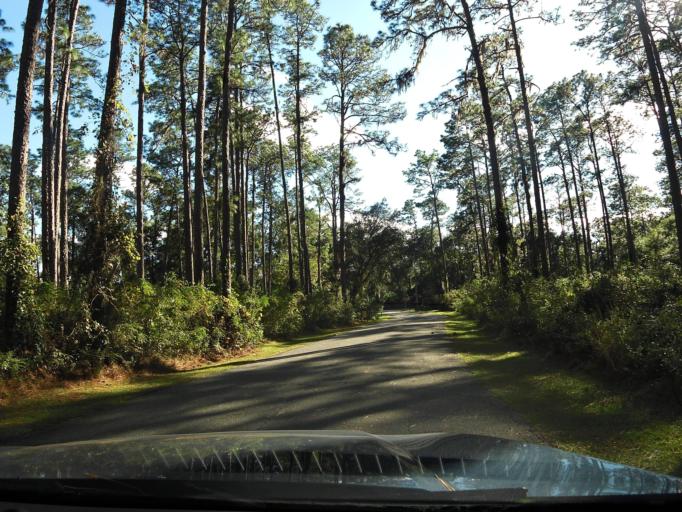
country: US
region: Florida
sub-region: Alachua County
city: Alachua
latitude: 29.7043
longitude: -82.3937
